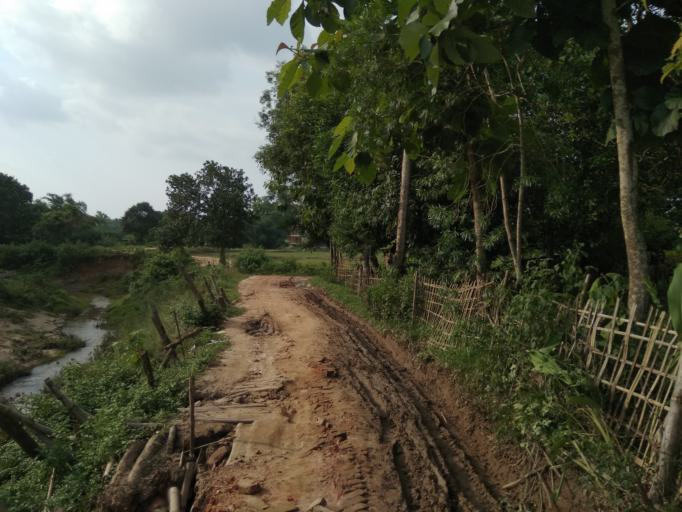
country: BD
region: Chittagong
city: Manikchari
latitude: 22.9331
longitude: 91.9105
